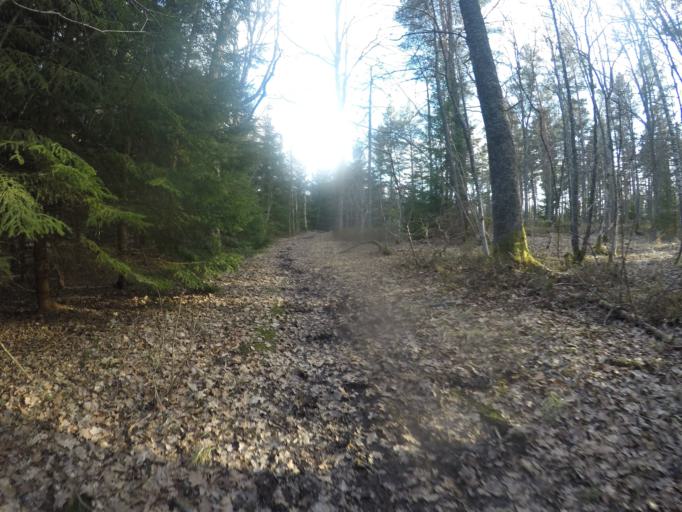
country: SE
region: Soedermanland
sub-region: Eskilstuna Kommun
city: Hallbybrunn
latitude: 59.3859
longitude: 16.4061
